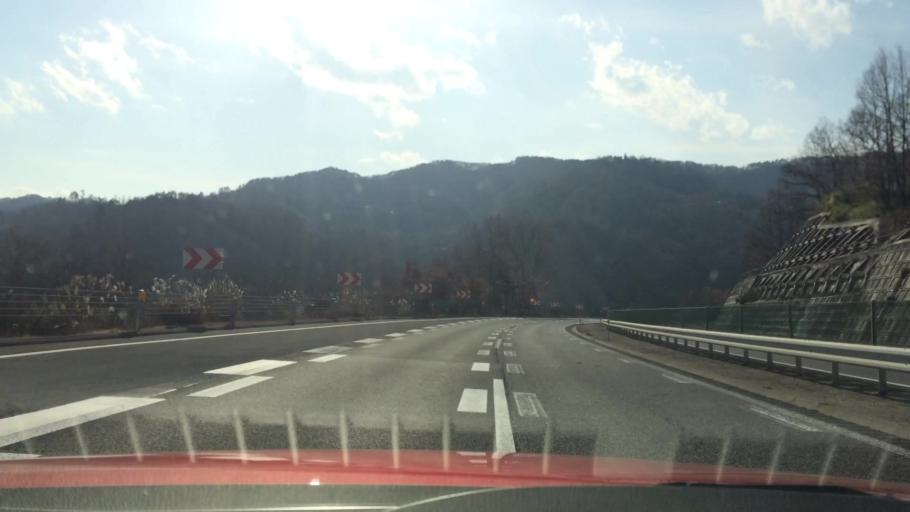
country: JP
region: Nagano
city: Toyoshina
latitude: 36.3465
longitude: 137.9623
